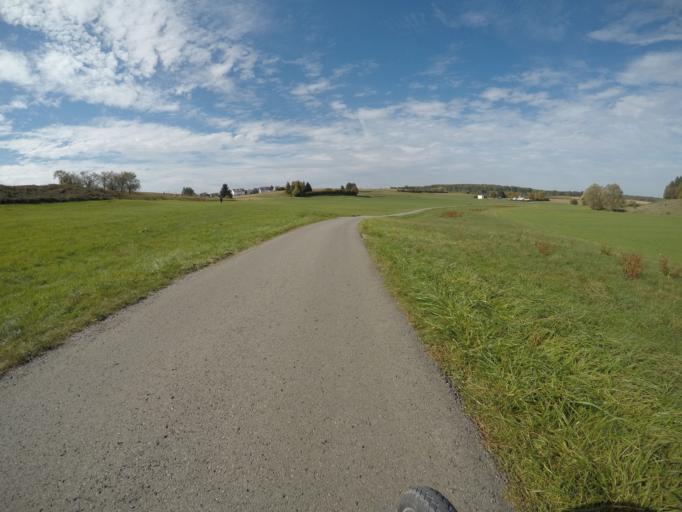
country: DE
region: Baden-Wuerttemberg
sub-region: Regierungsbezirk Stuttgart
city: Altdorf
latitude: 48.6294
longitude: 8.9832
